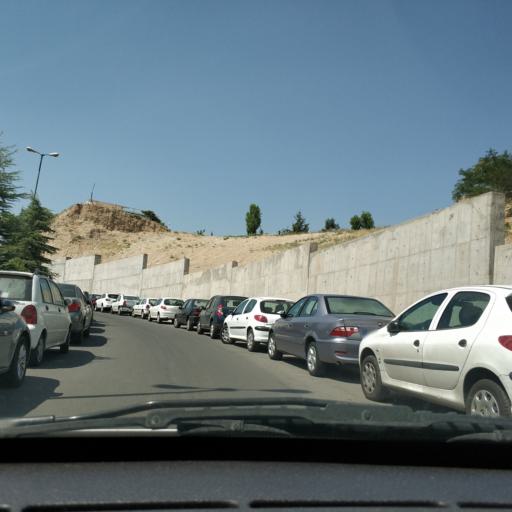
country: IR
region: Tehran
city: Tajrish
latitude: 35.7504
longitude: 51.4356
